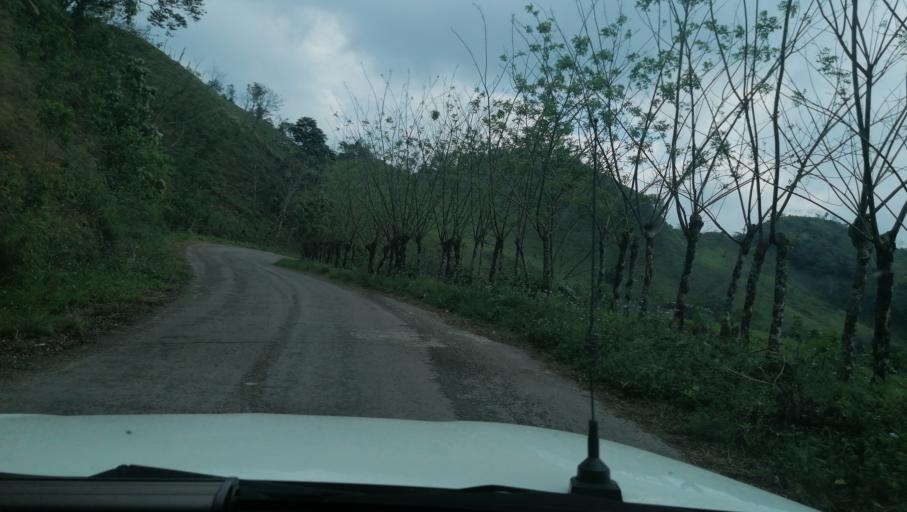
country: MX
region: Chiapas
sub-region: Francisco Leon
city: San Miguel la Sardina
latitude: 17.2390
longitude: -93.3054
